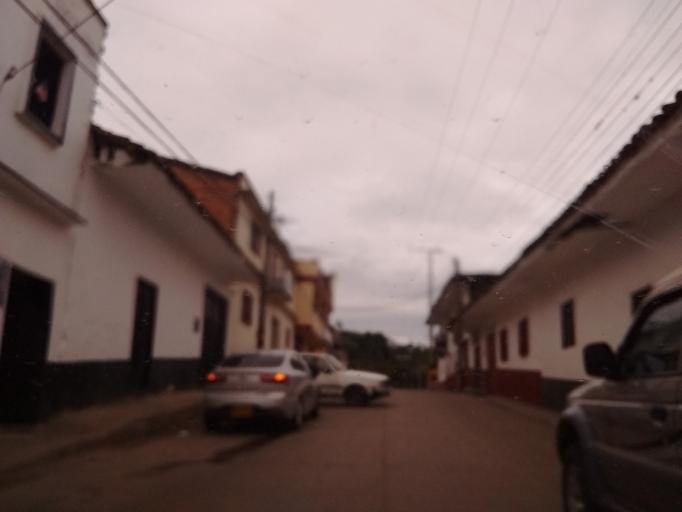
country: CO
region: Huila
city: San Agustin
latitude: 1.8836
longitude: -76.2720
